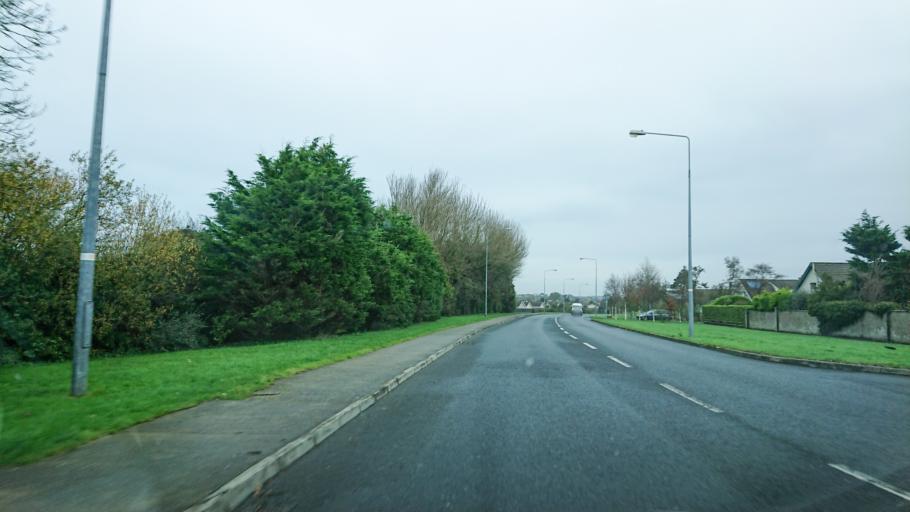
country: IE
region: Munster
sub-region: Waterford
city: Tra Mhor
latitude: 52.1579
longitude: -7.1695
